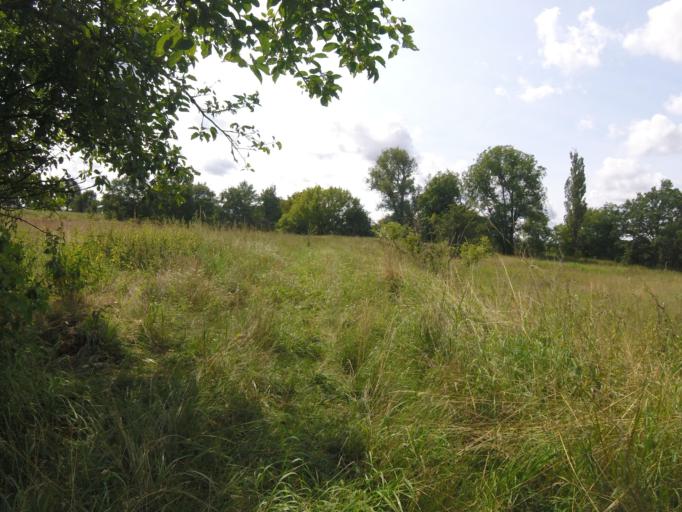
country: DE
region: Brandenburg
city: Mittenwalde
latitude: 52.2939
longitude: 13.5091
